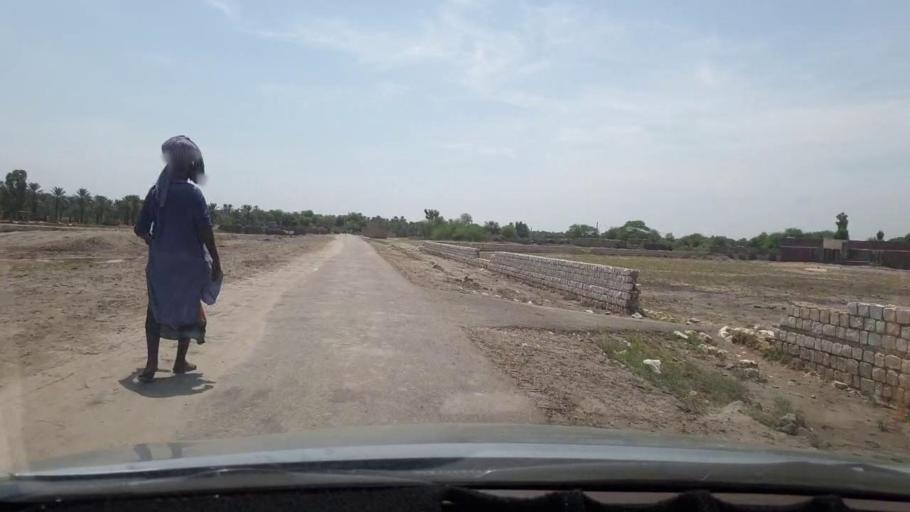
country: PK
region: Sindh
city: Khairpur
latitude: 27.4877
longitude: 68.7622
